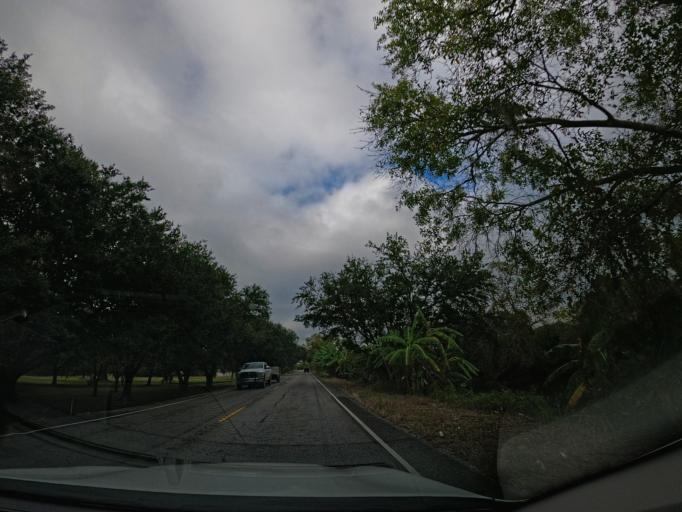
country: US
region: Louisiana
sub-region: Terrebonne Parish
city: Bayou Cane
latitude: 29.5713
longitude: -90.8051
